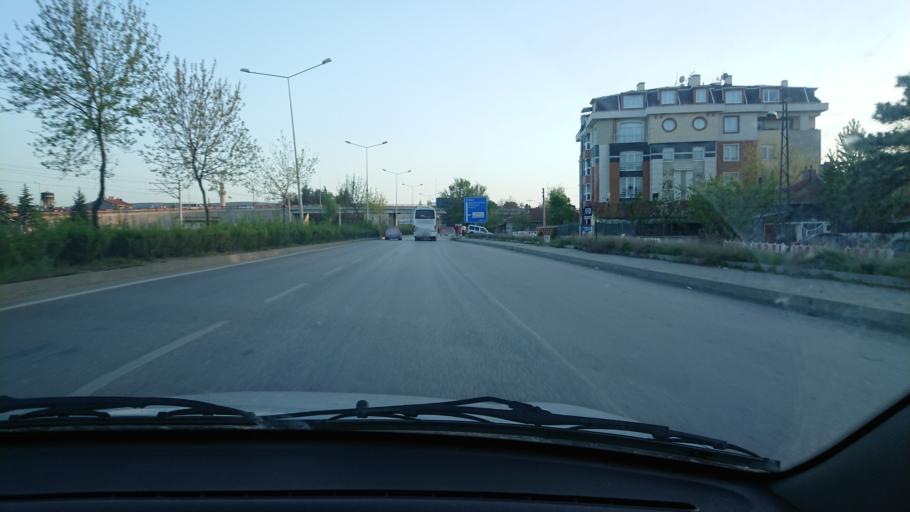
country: TR
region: Eskisehir
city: Eskisehir
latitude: 39.7703
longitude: 30.4822
